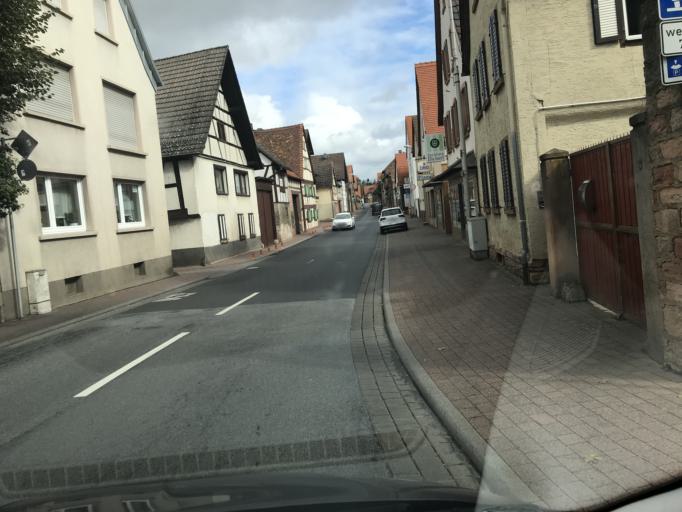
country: DE
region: Bavaria
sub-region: Regierungsbezirk Unterfranken
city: Grossostheim
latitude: 49.9090
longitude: 9.0594
